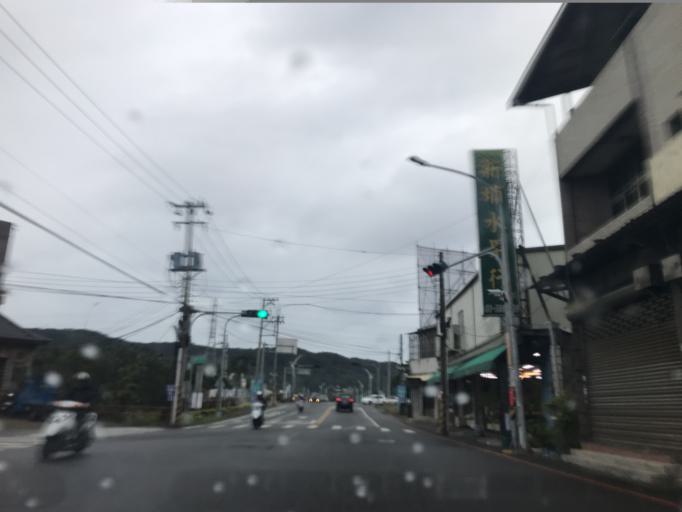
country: TW
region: Taiwan
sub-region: Hsinchu
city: Zhubei
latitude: 24.8273
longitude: 121.0685
